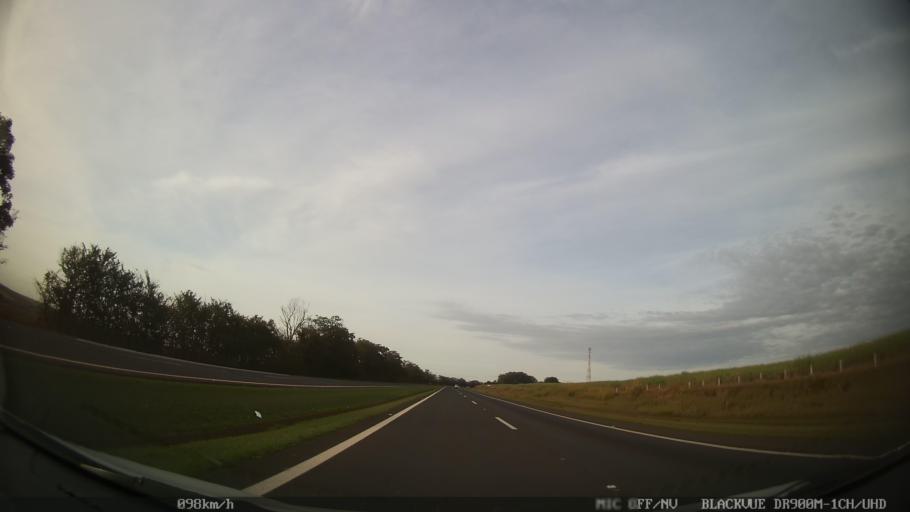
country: BR
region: Sao Paulo
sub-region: Iracemapolis
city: Iracemapolis
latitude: -22.6719
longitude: -47.5560
